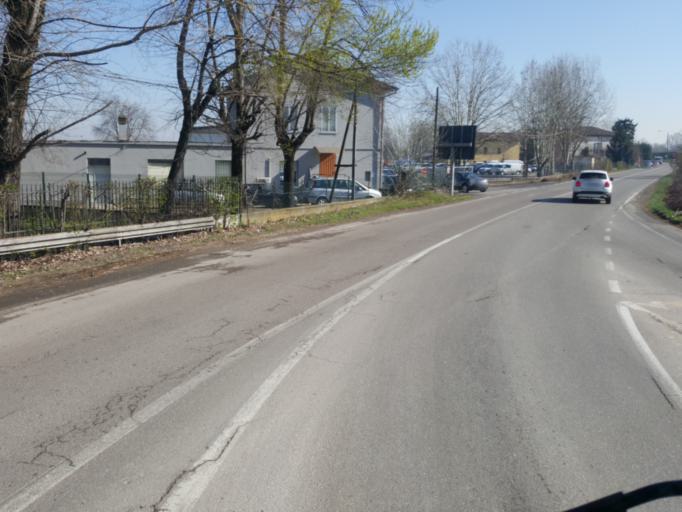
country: IT
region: Emilia-Romagna
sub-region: Provincia di Modena
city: Albareto
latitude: 44.6669
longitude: 10.9896
